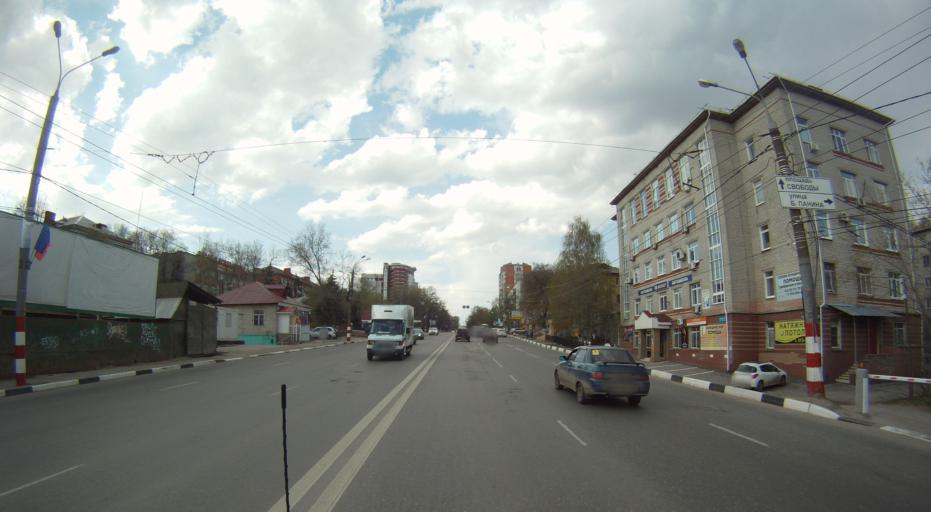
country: RU
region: Nizjnij Novgorod
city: Nizhniy Novgorod
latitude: 56.3073
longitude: 44.0244
